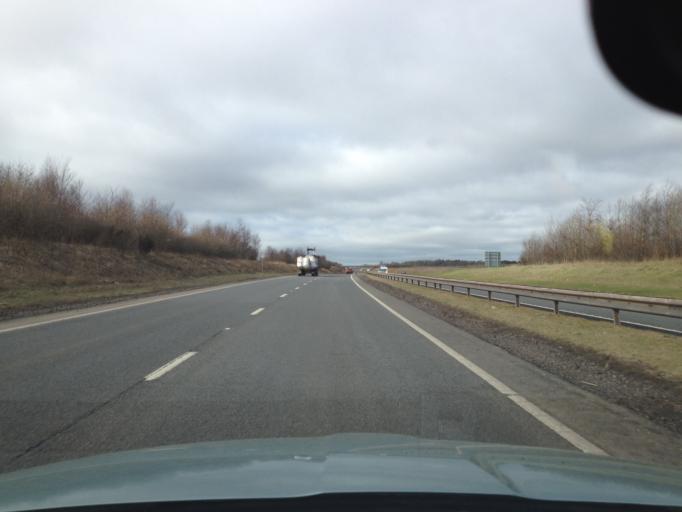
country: GB
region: Scotland
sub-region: East Lothian
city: Haddington
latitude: 55.9544
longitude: -2.8226
